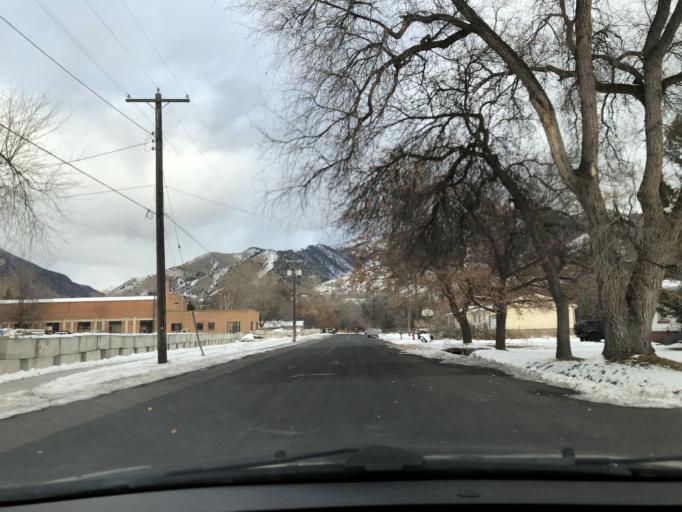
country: US
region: Utah
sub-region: Cache County
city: River Heights
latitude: 41.7293
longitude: -111.8200
